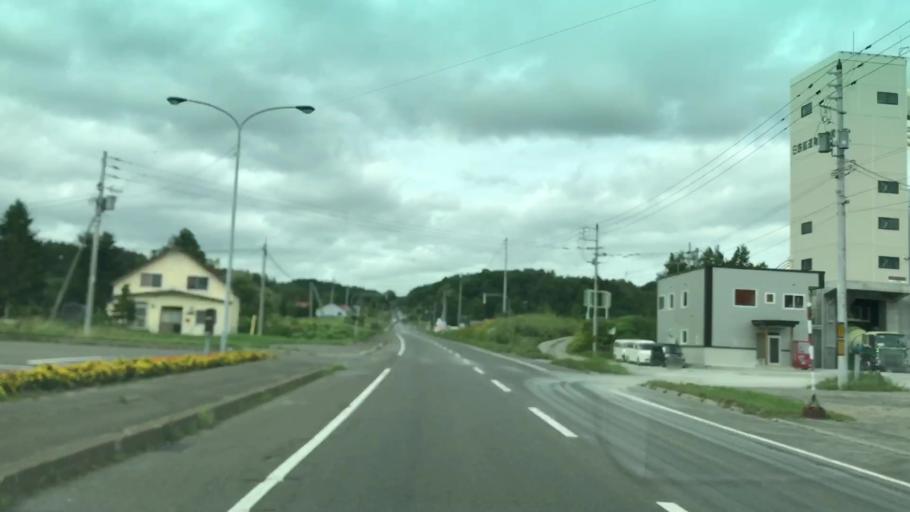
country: JP
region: Hokkaido
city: Niseko Town
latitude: 42.9204
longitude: 140.7418
